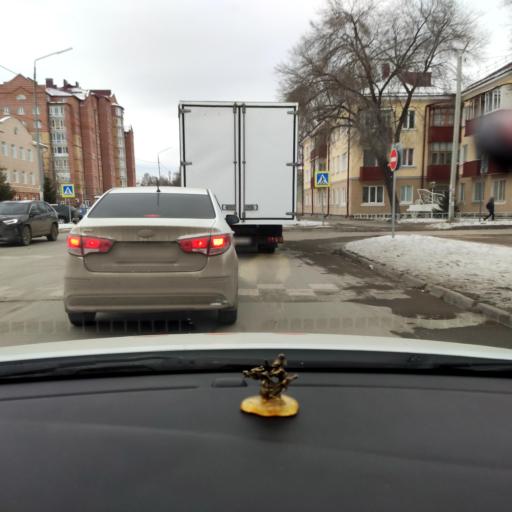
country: RU
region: Tatarstan
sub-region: Zelenodol'skiy Rayon
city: Zelenodolsk
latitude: 55.8502
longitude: 48.5106
